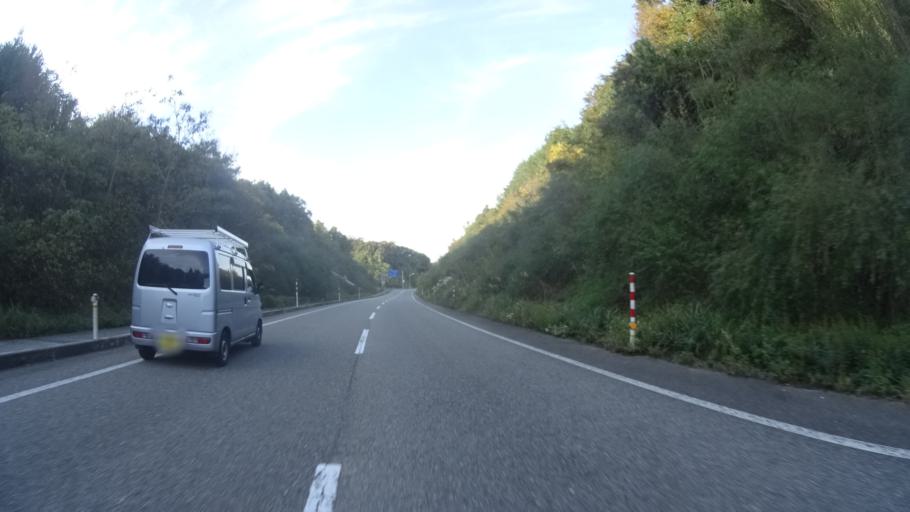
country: JP
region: Ishikawa
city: Hakui
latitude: 37.0759
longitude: 136.7300
